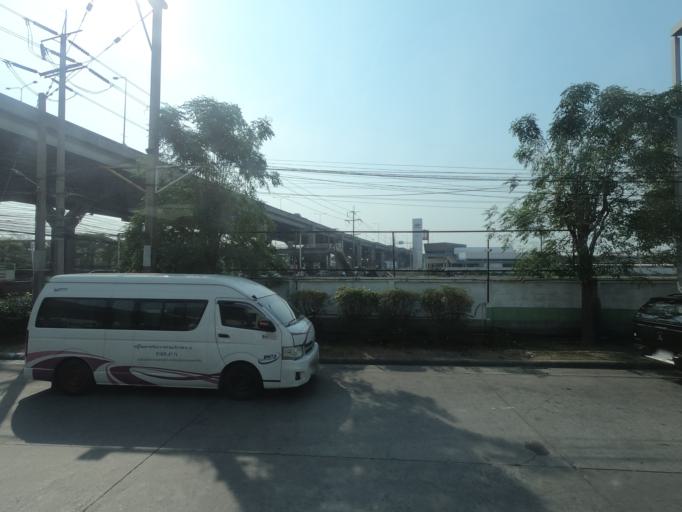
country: TH
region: Phra Nakhon Si Ayutthaya
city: Ban Bang Kadi Pathum Thani
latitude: 14.0003
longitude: 100.6112
